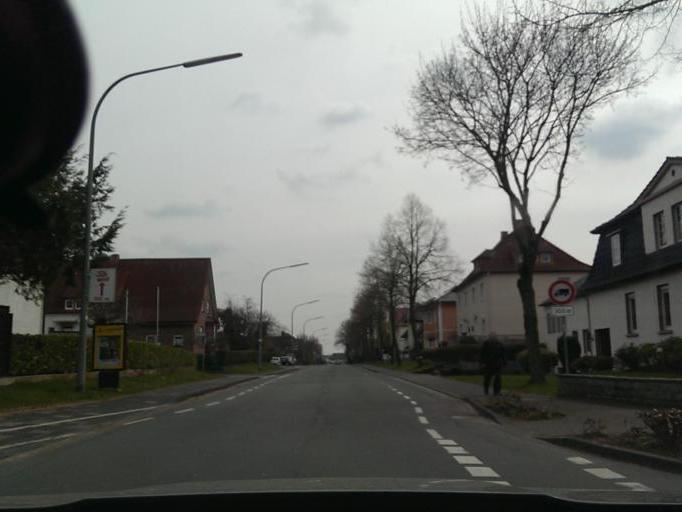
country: DE
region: North Rhine-Westphalia
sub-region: Regierungsbezirk Detmold
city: Delbruck
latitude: 51.7649
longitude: 8.5532
